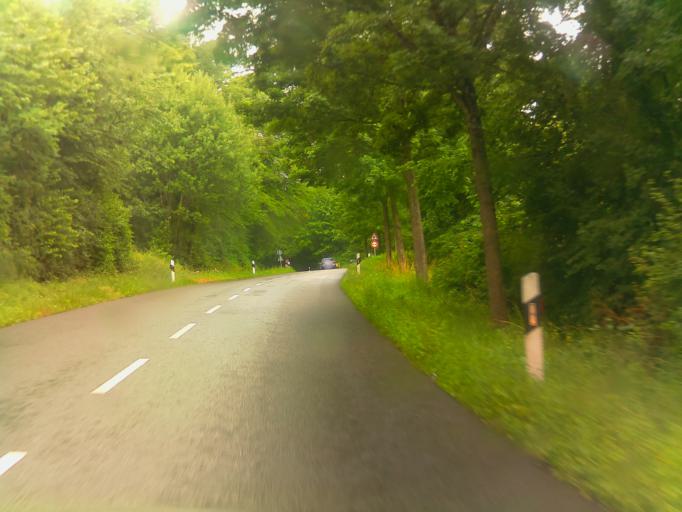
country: LU
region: Grevenmacher
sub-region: Canton de Remich
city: Mondorf-les-Bains
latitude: 49.5209
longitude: 6.2842
